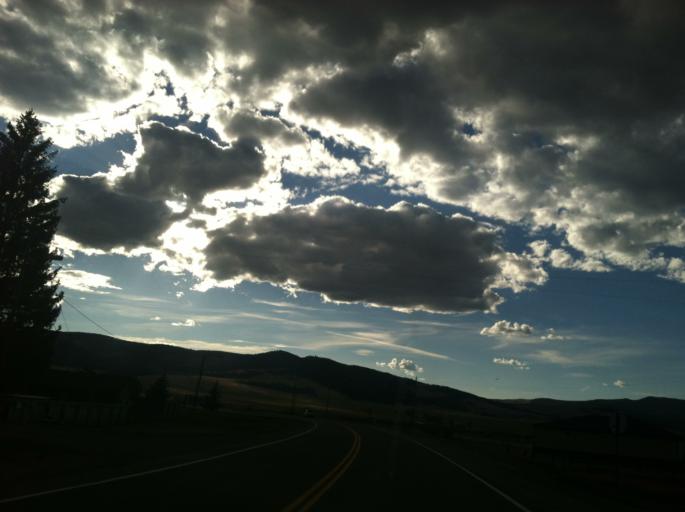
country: US
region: Montana
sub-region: Granite County
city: Philipsburg
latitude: 46.3349
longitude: -113.3059
